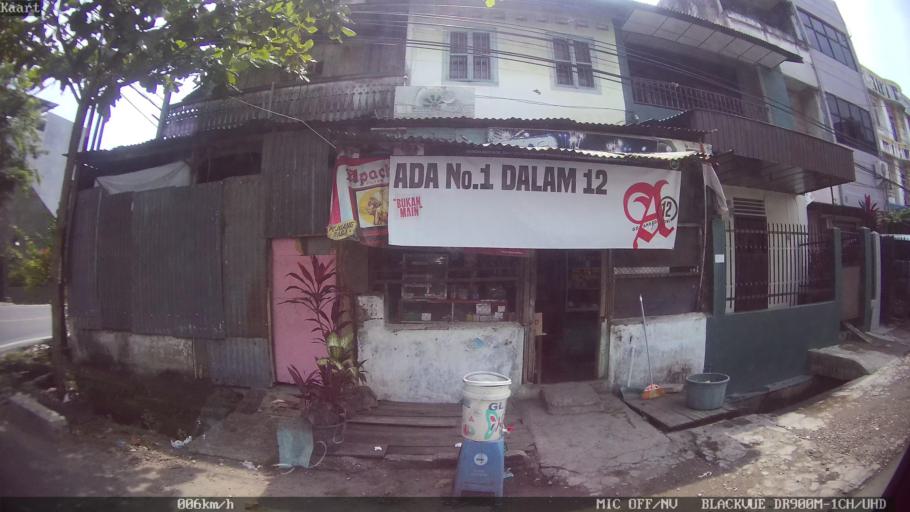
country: ID
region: Lampung
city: Bandarlampung
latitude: -5.4495
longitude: 105.2617
